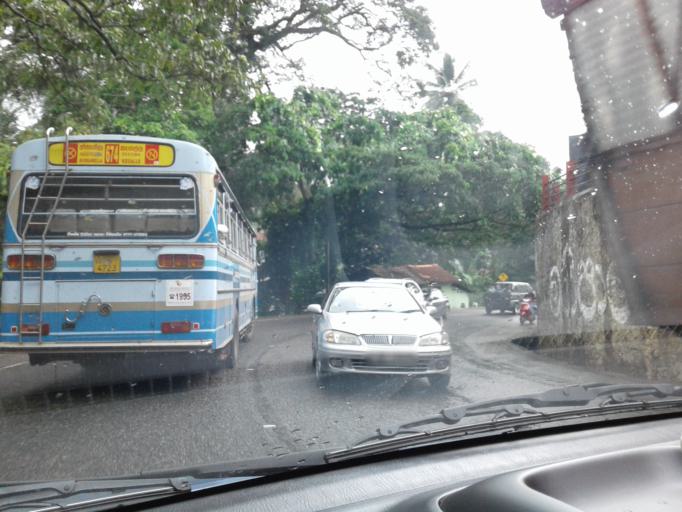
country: LK
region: Central
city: Kadugannawa
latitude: 7.2361
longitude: 80.3152
